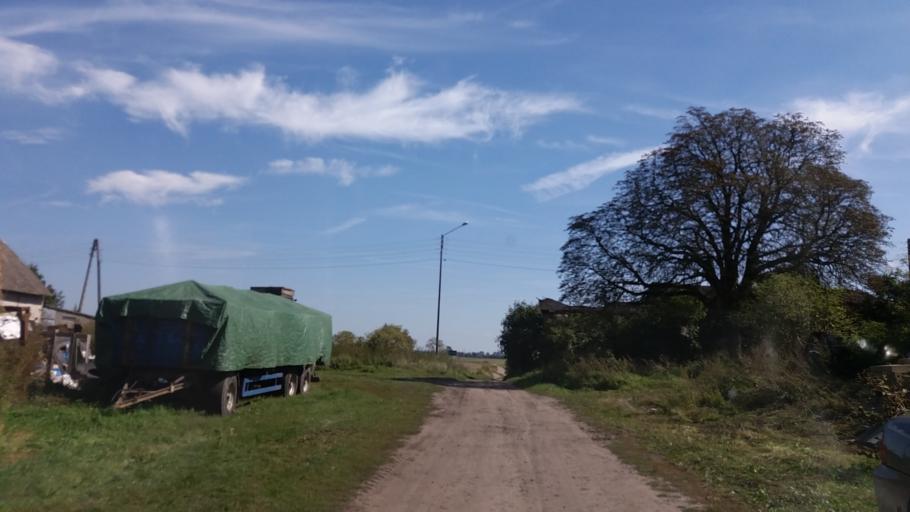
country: PL
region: West Pomeranian Voivodeship
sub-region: Powiat choszczenski
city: Choszczno
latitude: 53.1470
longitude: 15.4093
